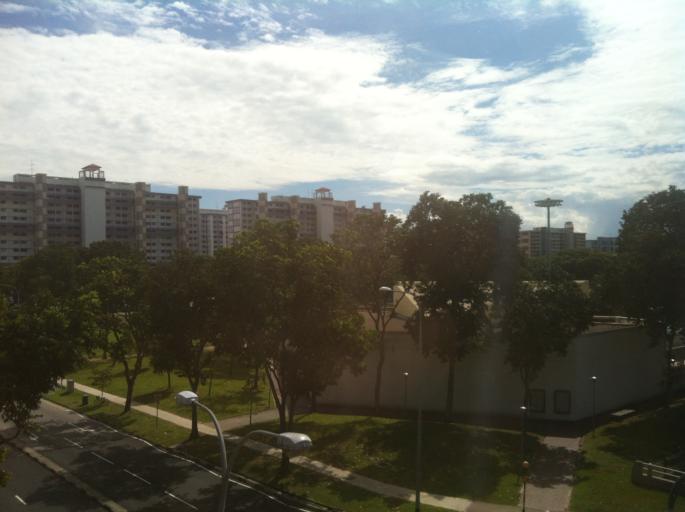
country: SG
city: Singapore
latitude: 1.3248
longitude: 103.9354
